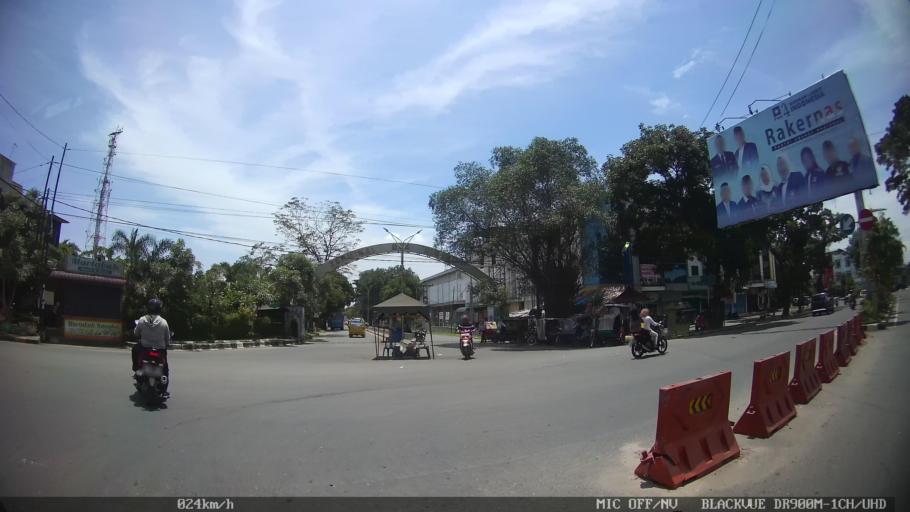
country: ID
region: North Sumatra
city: Binjai
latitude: 3.6094
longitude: 98.4949
